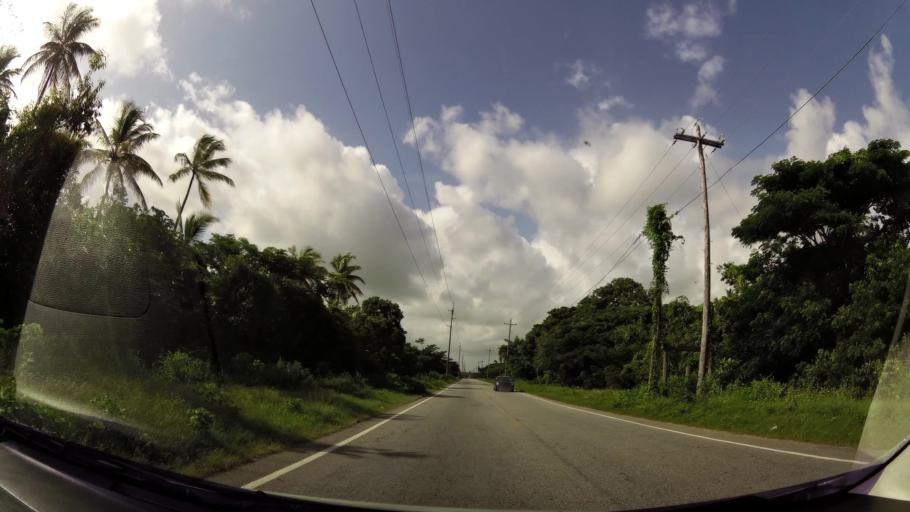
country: GY
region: Demerara-Mahaica
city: Mahaica Village
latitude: 6.6927
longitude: -57.9296
